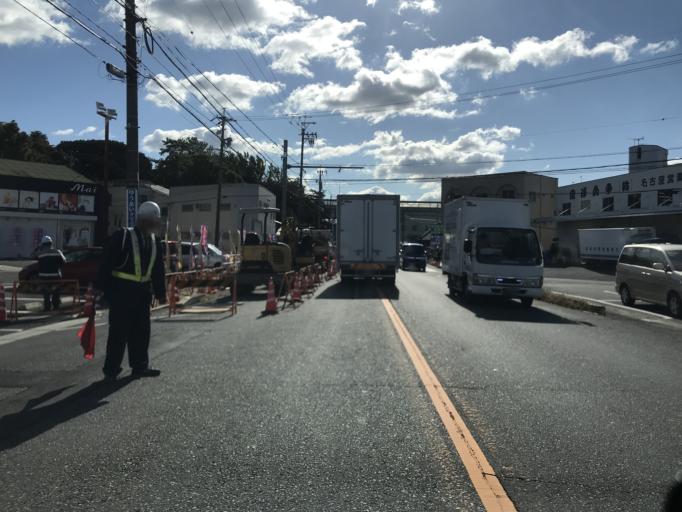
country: JP
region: Aichi
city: Inazawa
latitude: 35.2221
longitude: 136.8419
